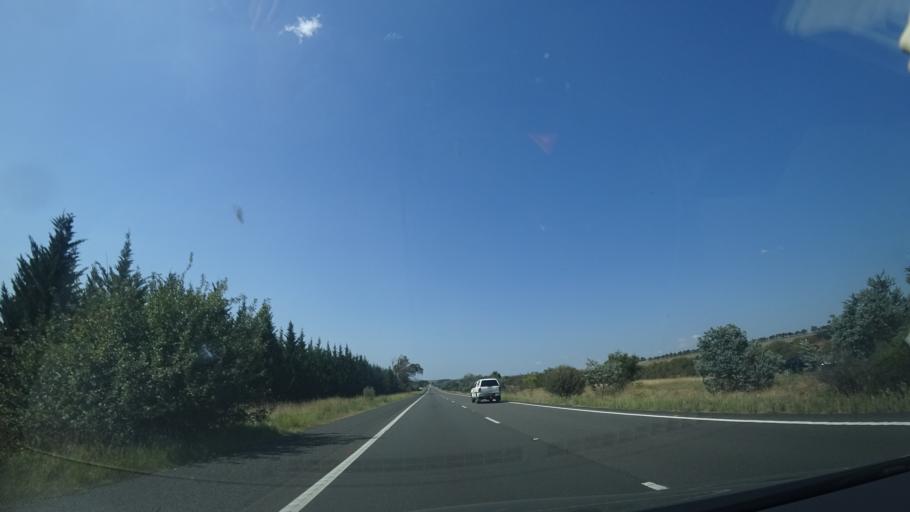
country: AU
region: New South Wales
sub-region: Wingecarribee
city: Moss Vale
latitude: -34.5483
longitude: 150.2701
